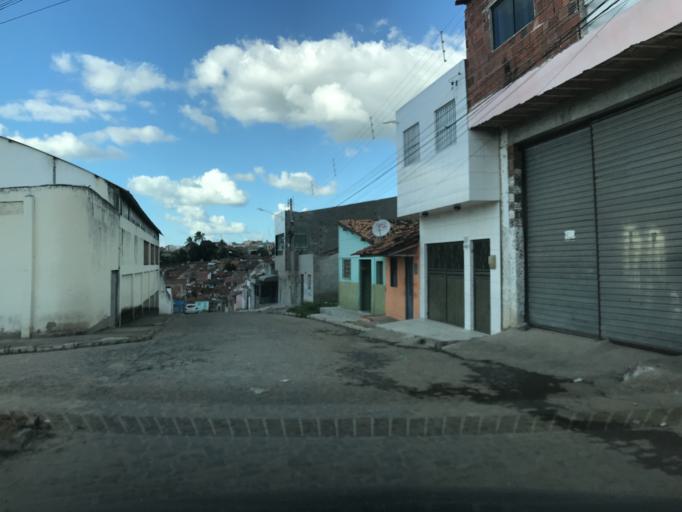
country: BR
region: Pernambuco
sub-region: Bezerros
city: Bezerros
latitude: -8.2425
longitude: -35.7579
